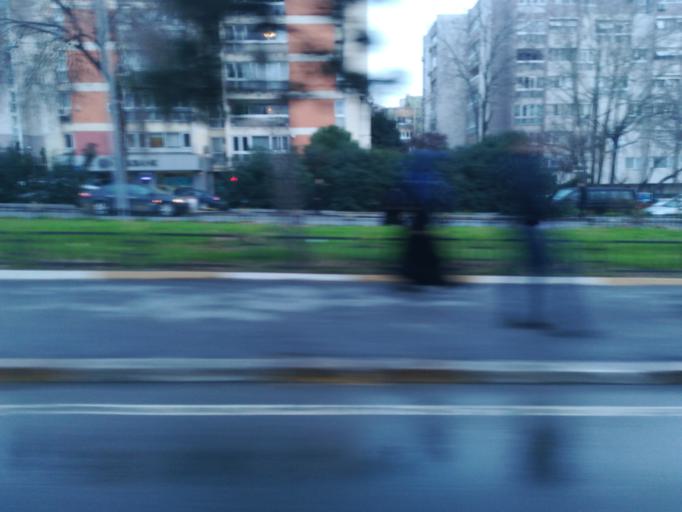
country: TR
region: Istanbul
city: Istanbul
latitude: 41.0229
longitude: 28.9321
